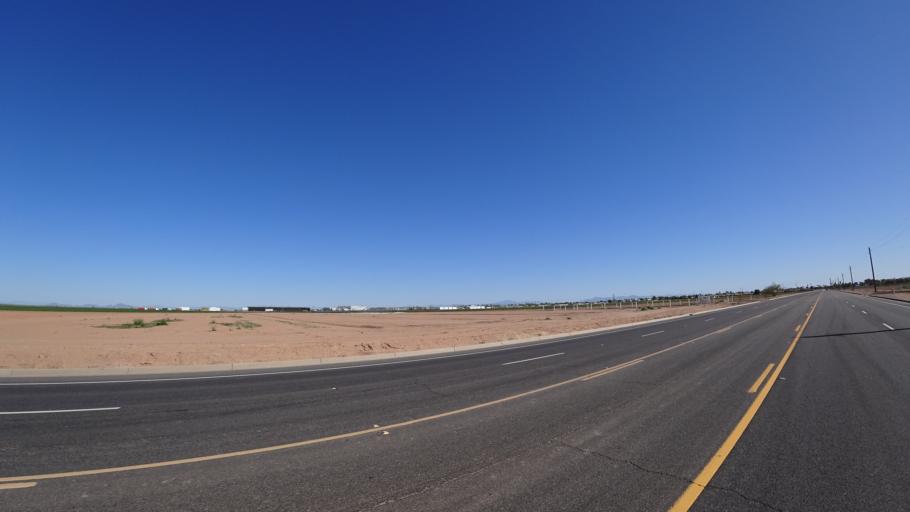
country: US
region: Arizona
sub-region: Maricopa County
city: Sun Lakes
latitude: 33.2192
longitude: -111.9023
